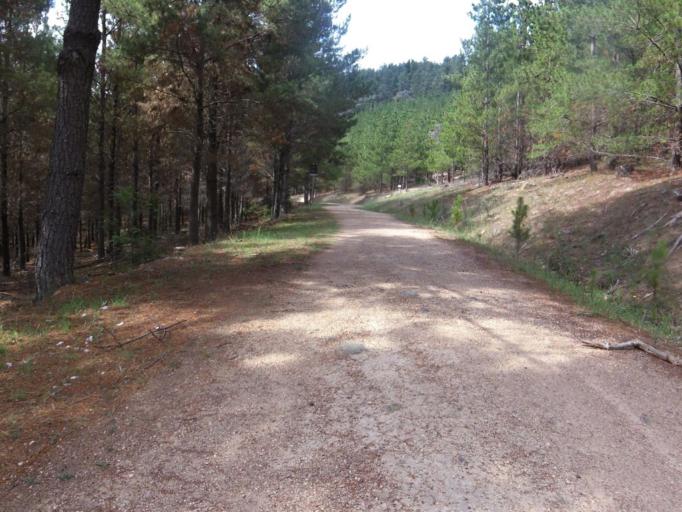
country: AU
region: Australian Capital Territory
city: Macarthur
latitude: -35.3820
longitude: 149.1209
